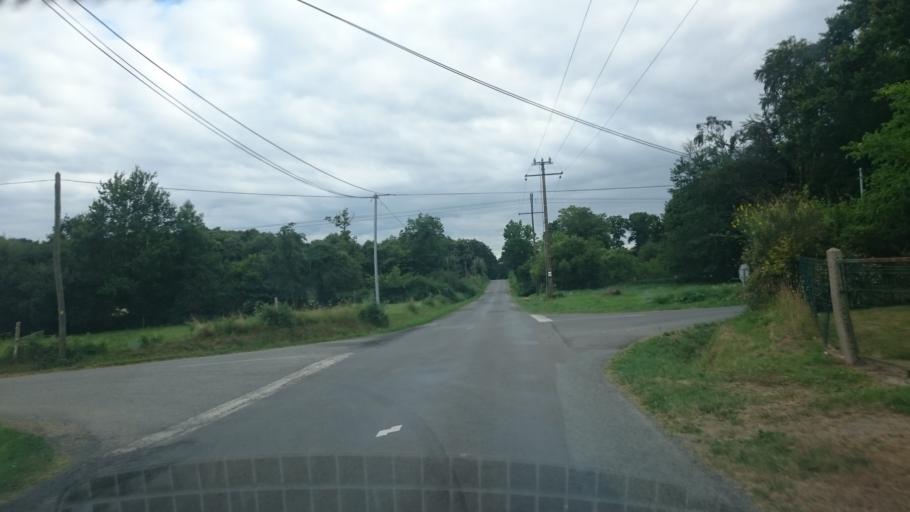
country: FR
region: Brittany
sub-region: Departement d'Ille-et-Vilaine
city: Meillac
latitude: 48.4337
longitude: -1.8346
